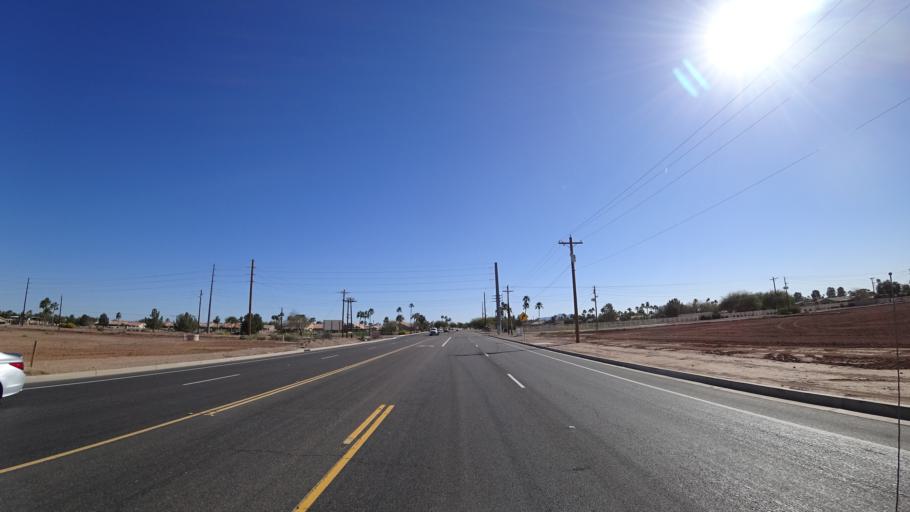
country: US
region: Arizona
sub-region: Maricopa County
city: Sun Lakes
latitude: 33.2192
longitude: -111.8943
